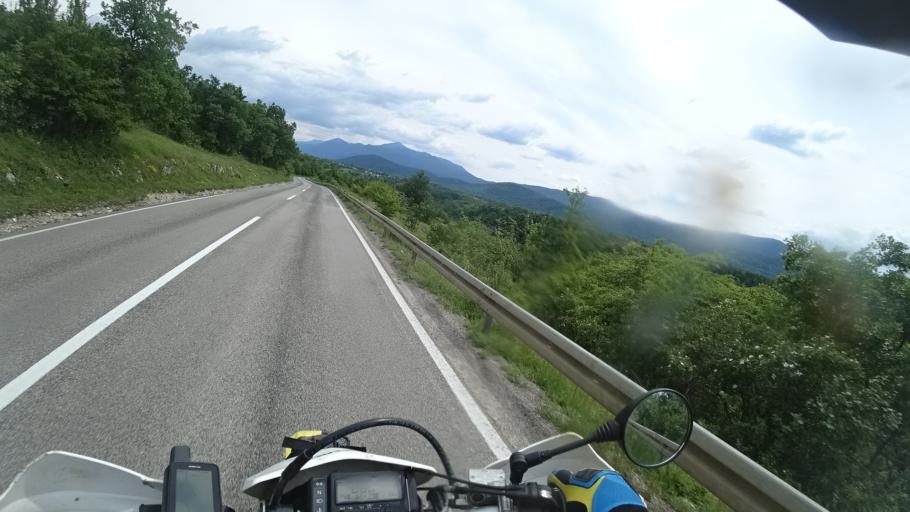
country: HR
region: Licko-Senjska
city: Jezerce
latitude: 44.9256
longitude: 15.7030
